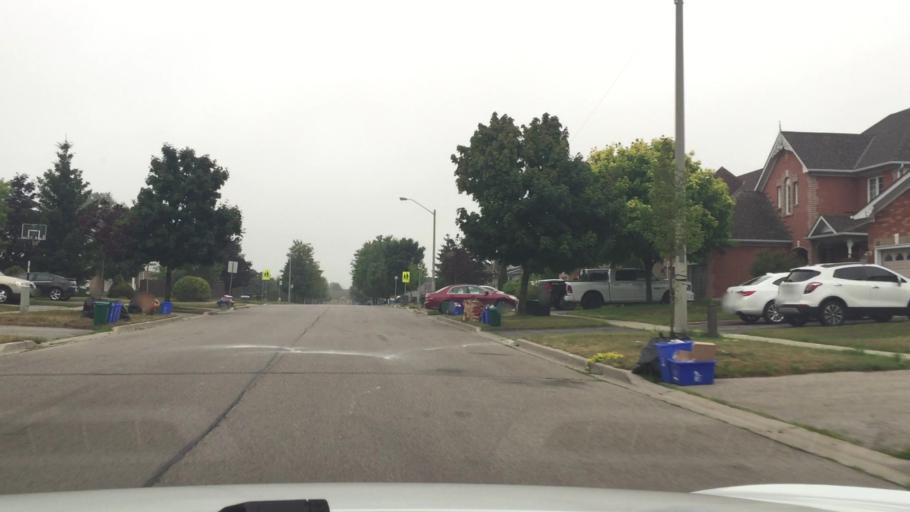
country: CA
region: Ontario
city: Oshawa
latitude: 43.9049
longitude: -78.7813
